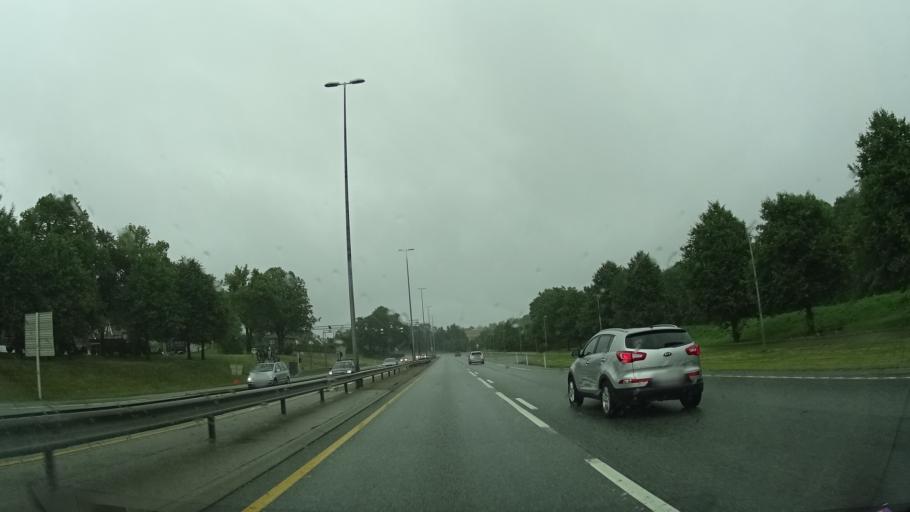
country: NO
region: Vest-Agder
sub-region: Kristiansand
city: Kristiansand
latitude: 58.1617
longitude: 8.0216
